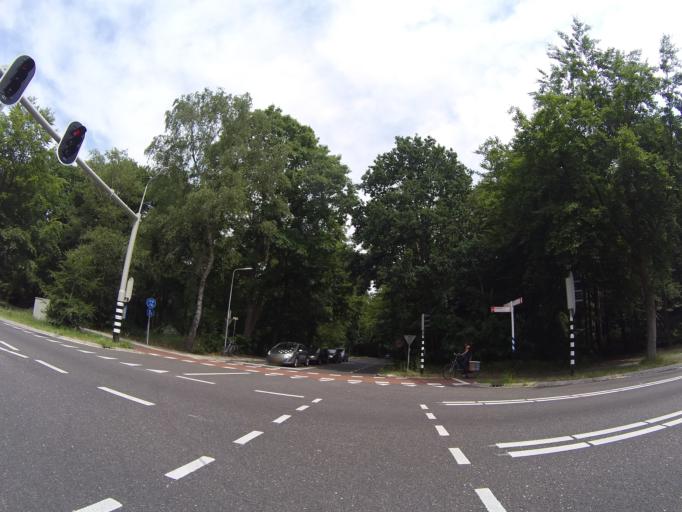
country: NL
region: Utrecht
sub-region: Gemeente Zeist
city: Zeist
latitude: 52.0731
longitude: 5.2507
